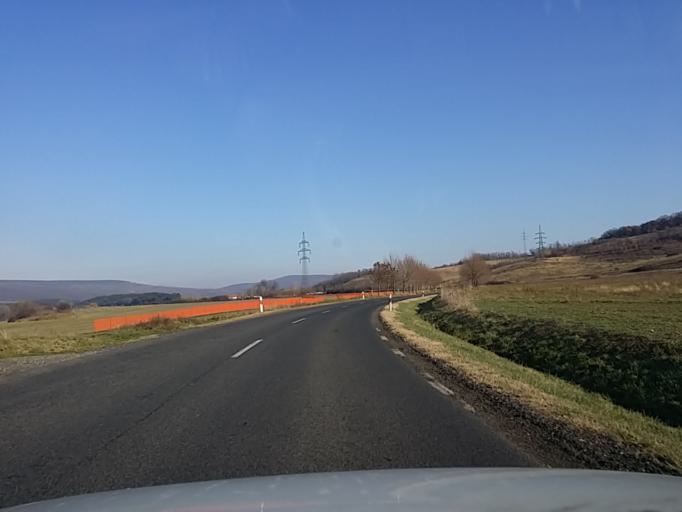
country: HU
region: Veszprem
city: Tapolca
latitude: 46.9024
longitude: 17.5236
